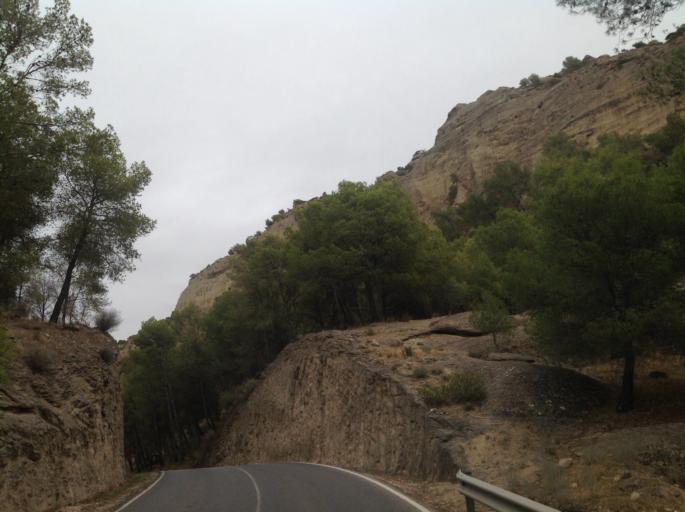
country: ES
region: Andalusia
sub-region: Provincia de Malaga
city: Ardales
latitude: 36.9187
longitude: -4.8030
